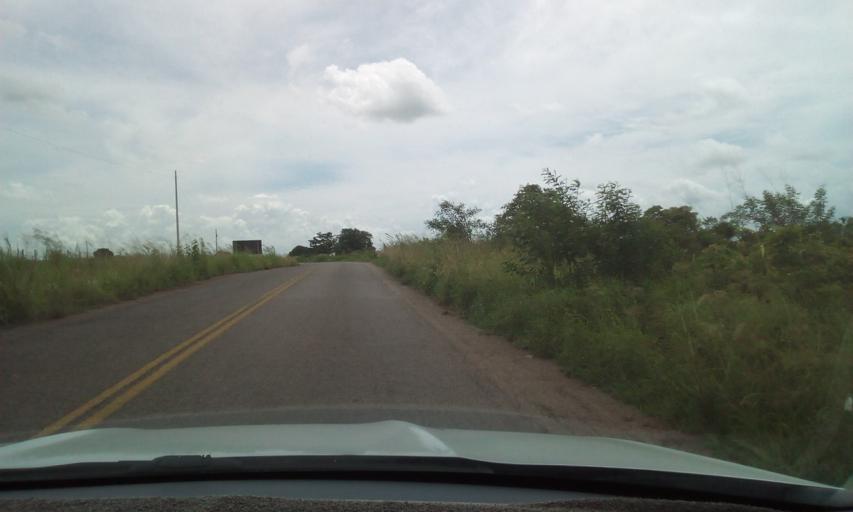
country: BR
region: Paraiba
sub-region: Mari
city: Mari
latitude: -7.0934
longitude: -35.3204
